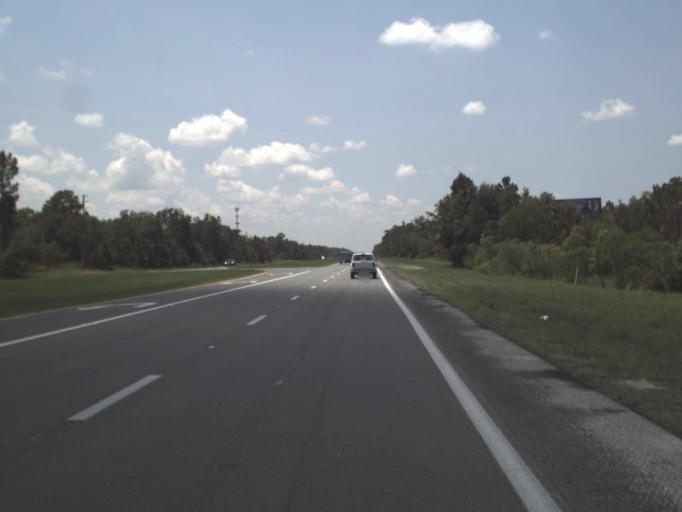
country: US
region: Florida
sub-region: Hernando County
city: North Weeki Wachee
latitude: 28.6322
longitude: -82.5521
